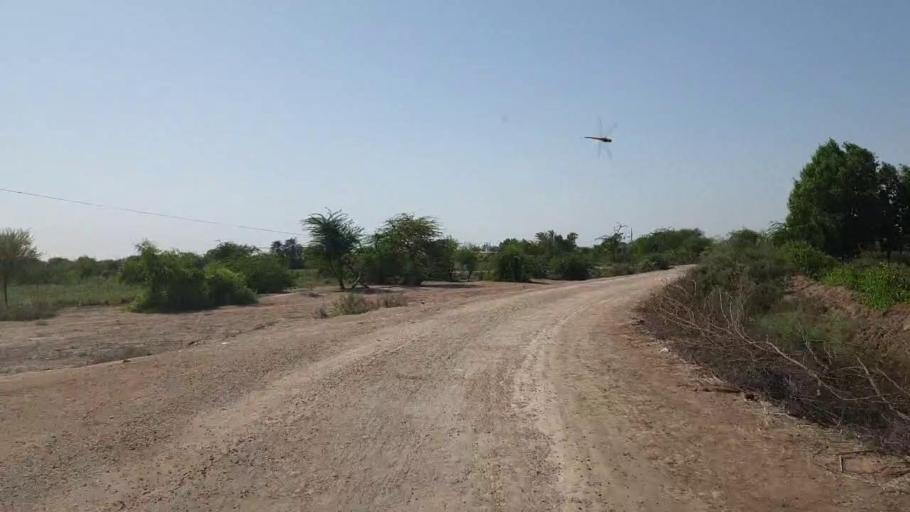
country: PK
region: Sindh
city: Tando Bago
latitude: 24.7049
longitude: 69.0394
